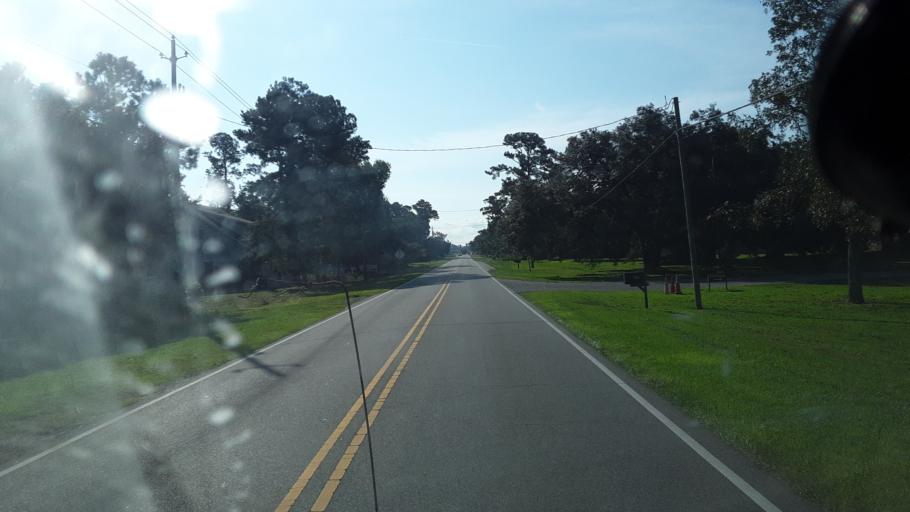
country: US
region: North Carolina
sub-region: Brunswick County
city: Navassa
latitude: 34.2410
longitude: -78.0116
